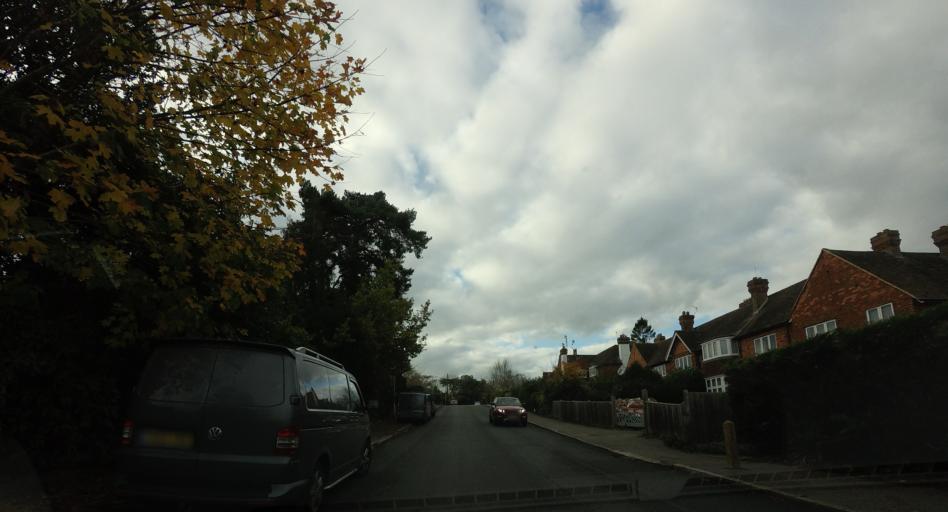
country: GB
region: England
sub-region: Kent
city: Tonbridge
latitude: 51.2032
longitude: 0.2843
